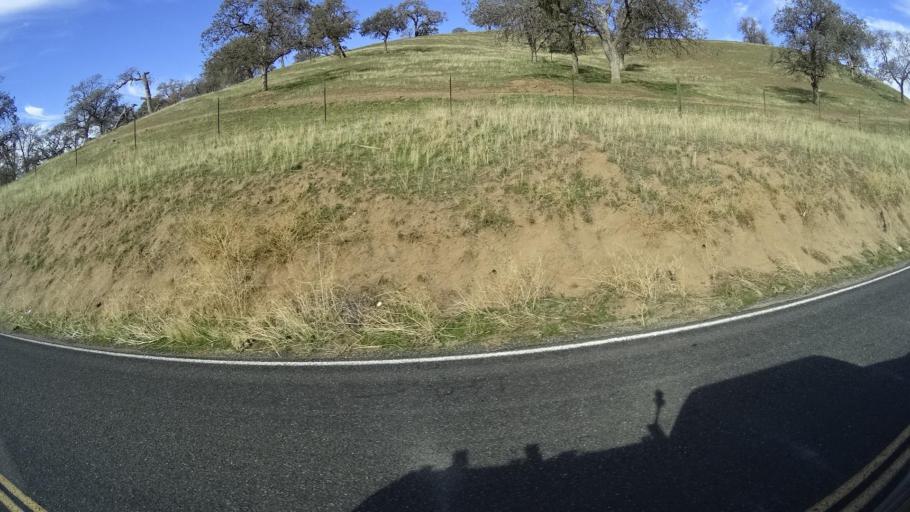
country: US
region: California
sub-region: Kern County
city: Alta Sierra
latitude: 35.6277
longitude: -118.8024
